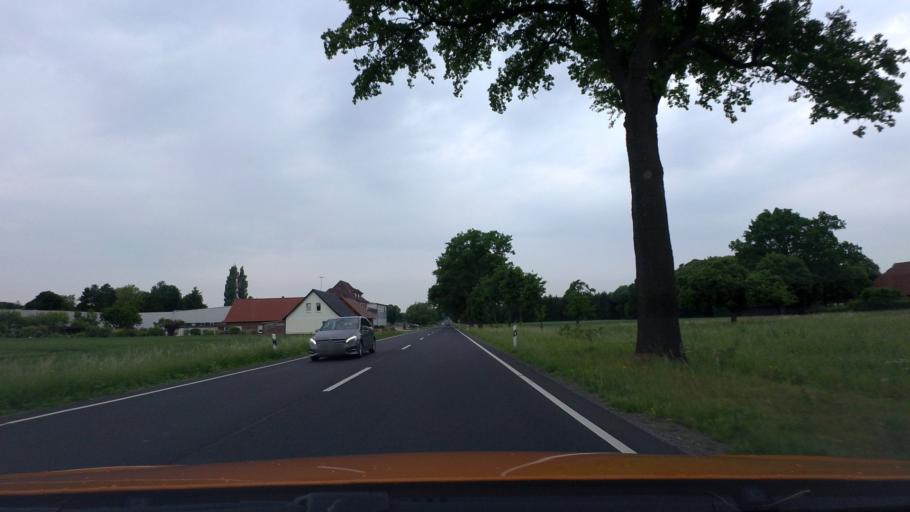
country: DE
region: Lower Saxony
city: Wietzen
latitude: 52.6992
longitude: 9.0848
